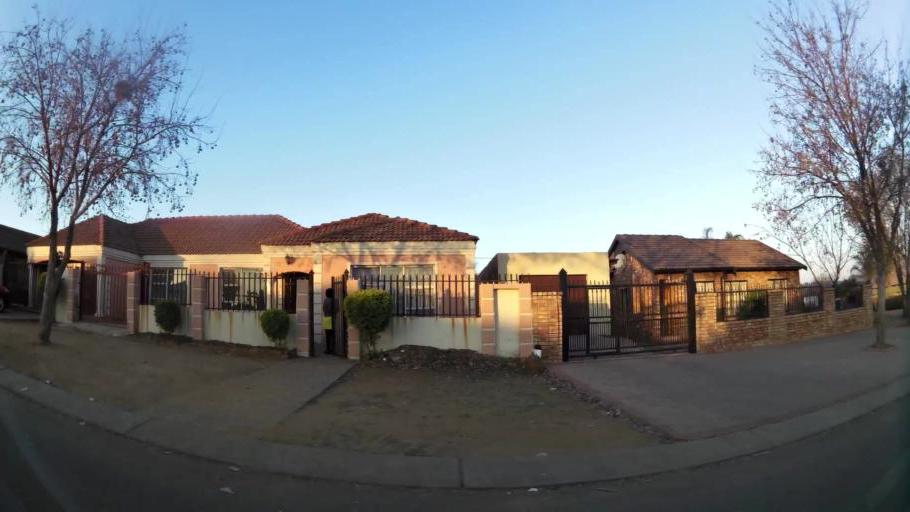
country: ZA
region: Gauteng
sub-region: City of Tshwane Metropolitan Municipality
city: Pretoria
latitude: -25.7432
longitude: 28.1389
